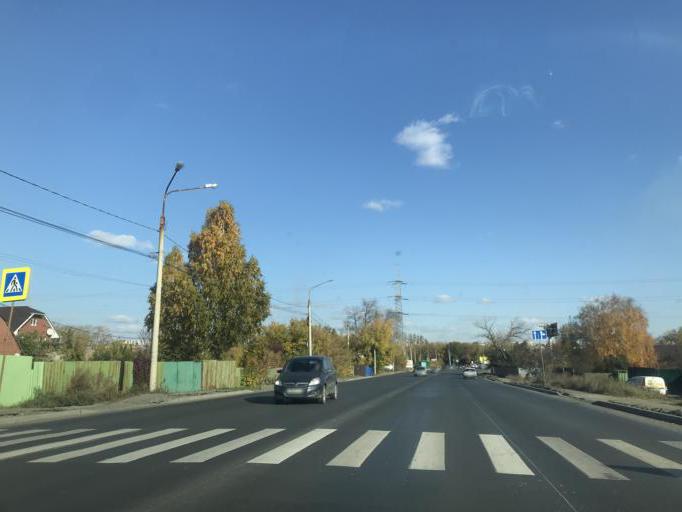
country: RU
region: Chelyabinsk
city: Dolgoderevenskoye
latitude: 55.2410
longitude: 61.3560
